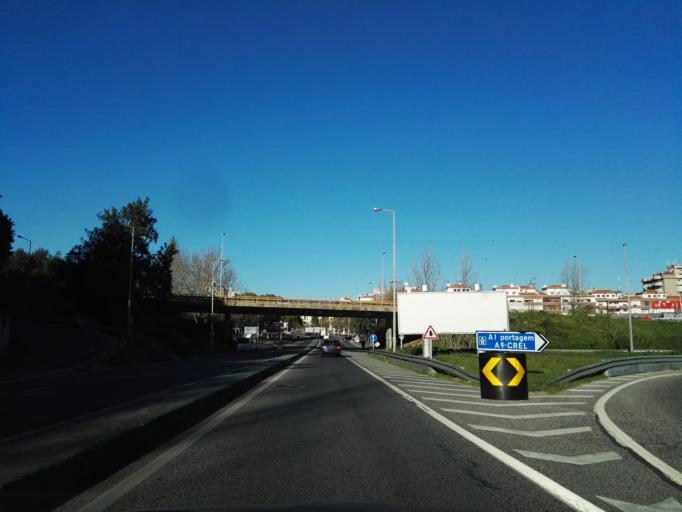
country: PT
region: Lisbon
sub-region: Vila Franca de Xira
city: Vialonga
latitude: 38.8898
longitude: -9.0437
